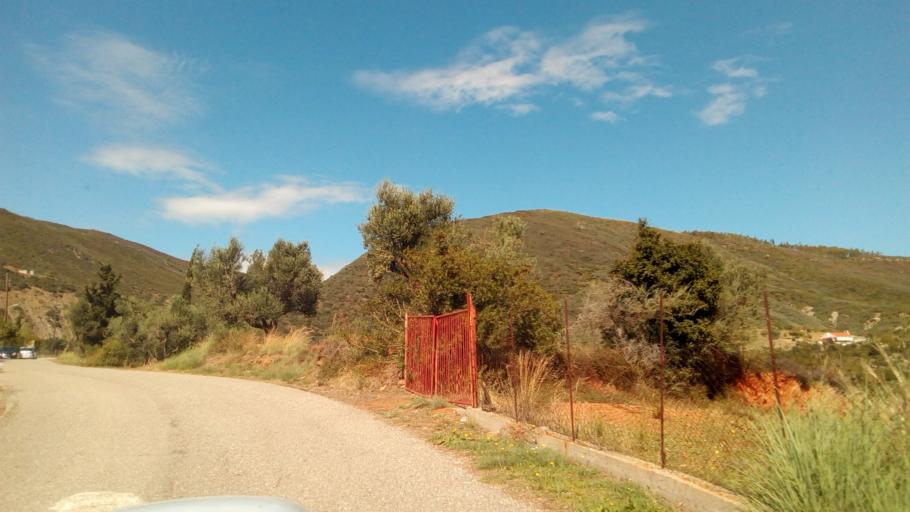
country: GR
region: West Greece
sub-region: Nomos Aitolias kai Akarnanias
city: Antirrio
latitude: 38.3705
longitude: 21.7762
